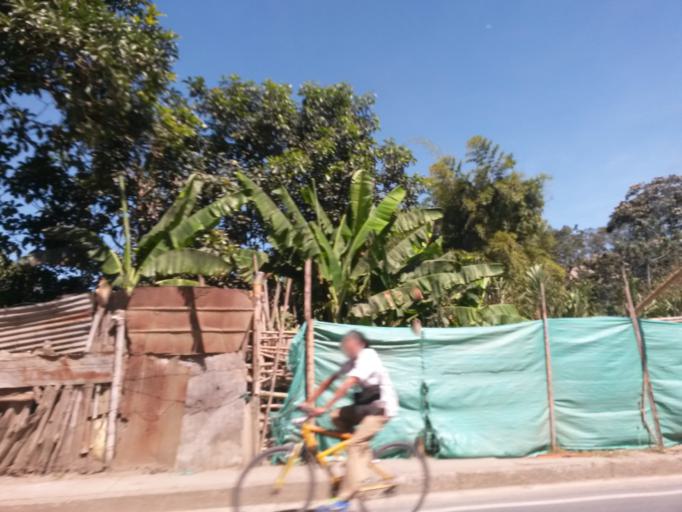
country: CO
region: Cauca
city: Popayan
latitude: 2.4562
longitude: -76.6428
